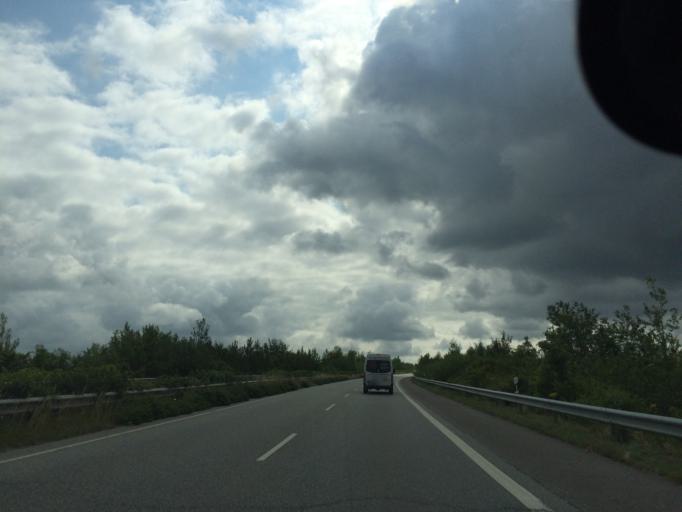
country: DE
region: Schleswig-Holstein
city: Ottendorf
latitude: 54.3729
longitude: 10.0668
